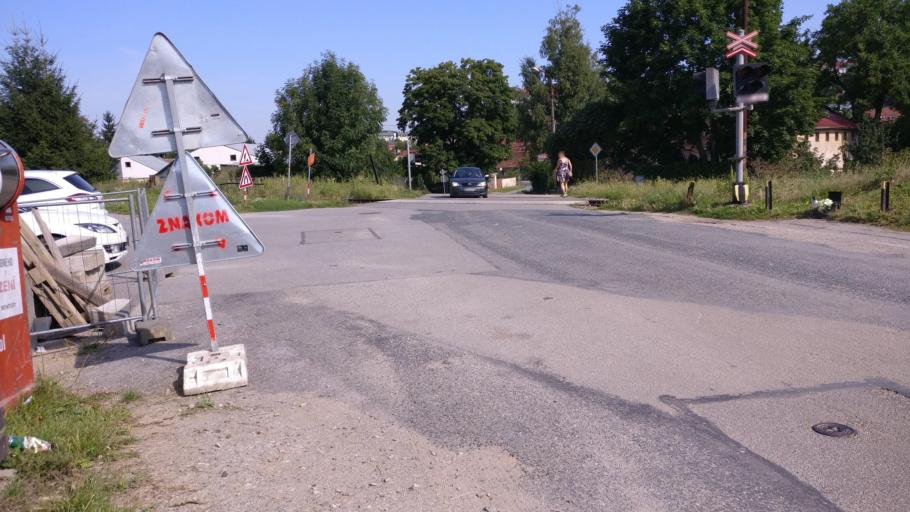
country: CZ
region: South Moravian
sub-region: Okres Brno-Venkov
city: Rosice
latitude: 49.1773
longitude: 16.3872
